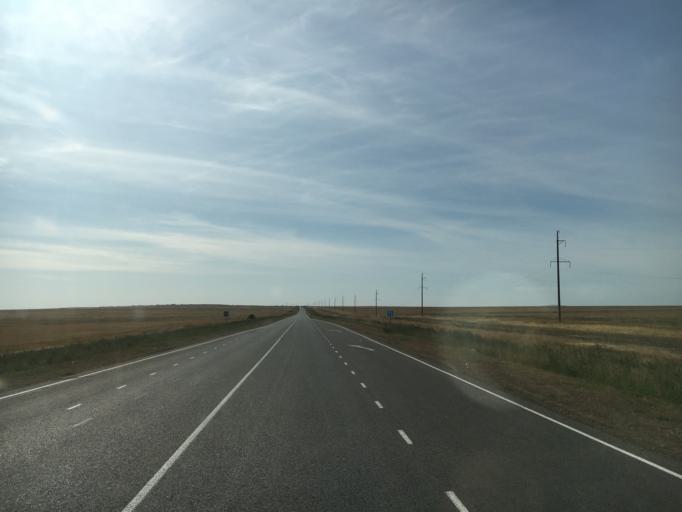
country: KZ
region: Batys Qazaqstan
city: Peremetnoe
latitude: 51.1170
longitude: 50.6214
